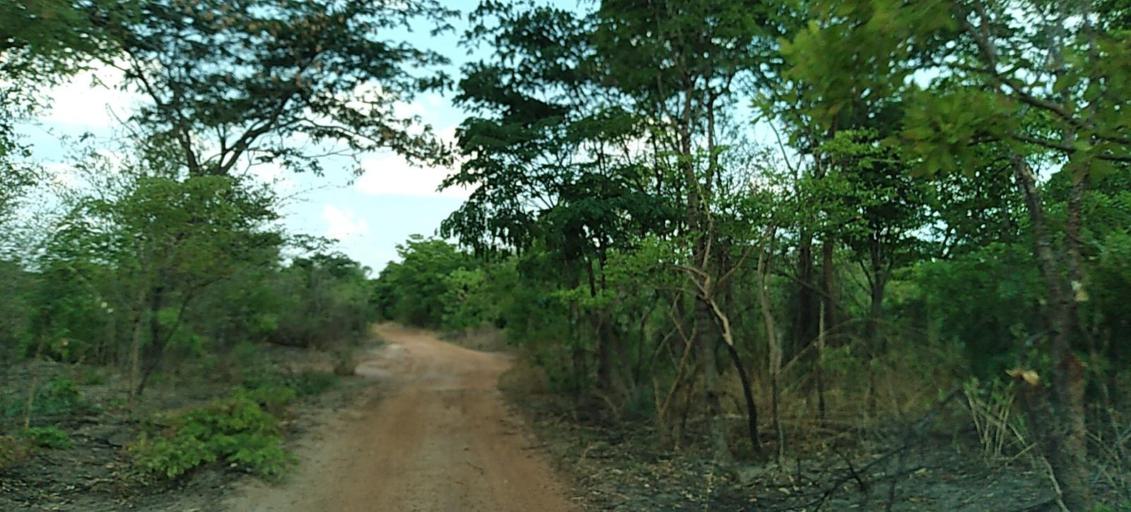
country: ZM
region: Copperbelt
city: Luanshya
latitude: -13.1556
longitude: 28.3246
